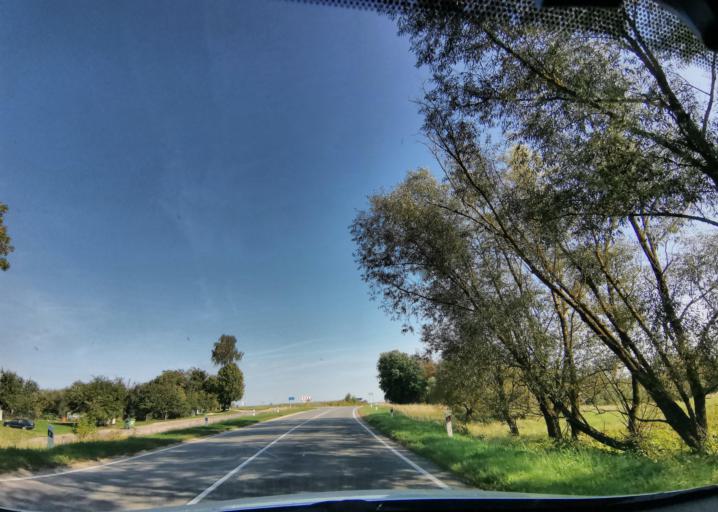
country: RU
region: Kaliningrad
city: Neman
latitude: 55.0171
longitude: 22.1131
